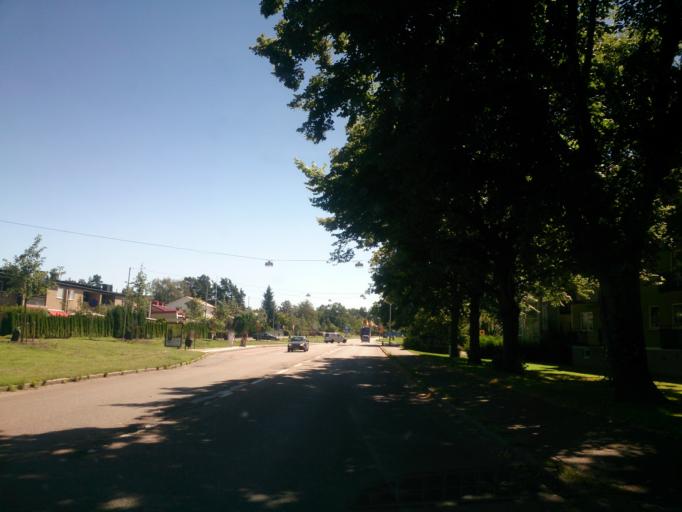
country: SE
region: OEstergoetland
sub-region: Linkopings Kommun
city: Linkoping
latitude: 58.3959
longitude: 15.6416
